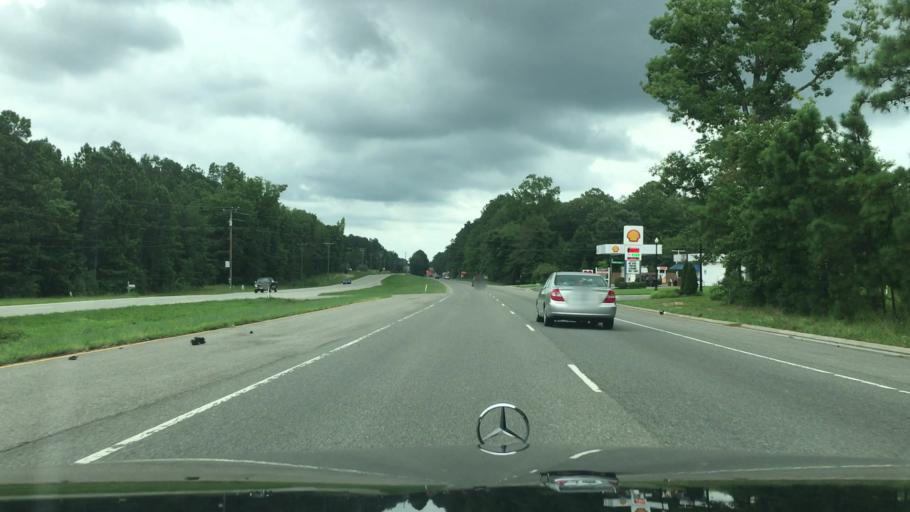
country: US
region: Virginia
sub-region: Chesterfield County
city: Woodlake
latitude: 37.3938
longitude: -77.7235
